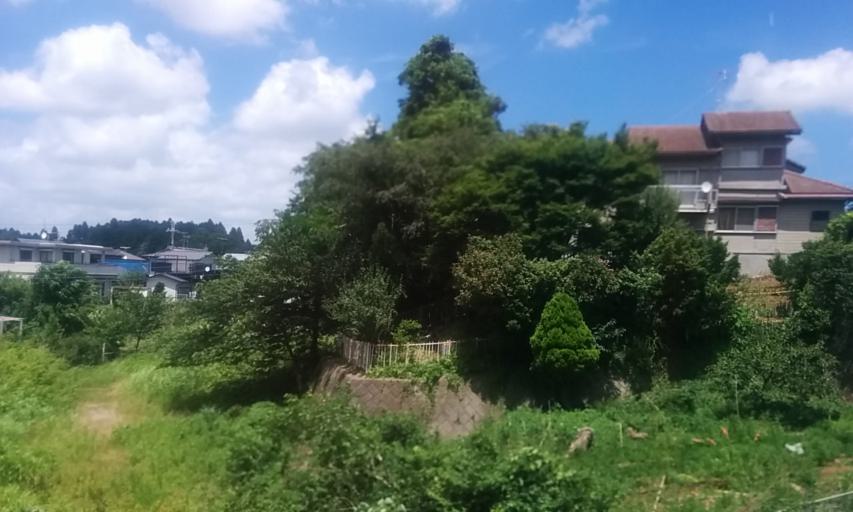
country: JP
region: Chiba
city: Oami
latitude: 35.5336
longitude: 140.2616
